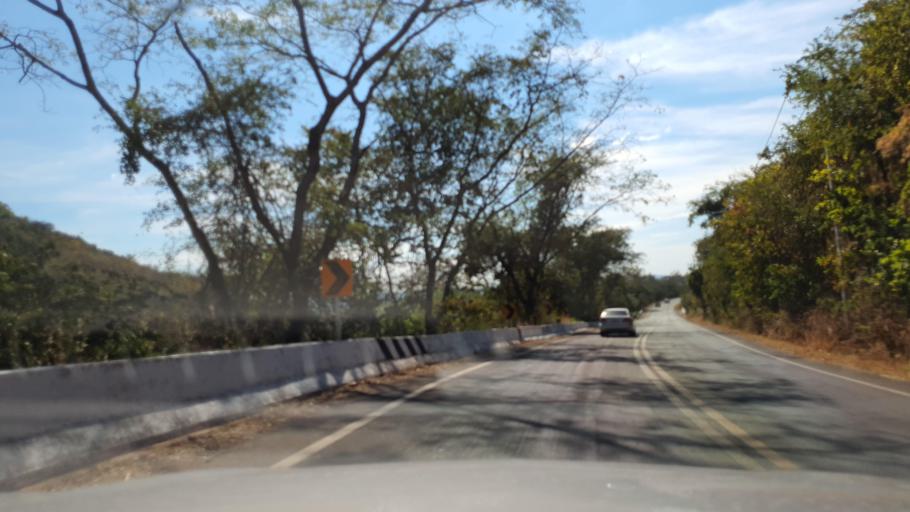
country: TH
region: Kalasin
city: Khao Wong
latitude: 16.7574
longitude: 104.1280
